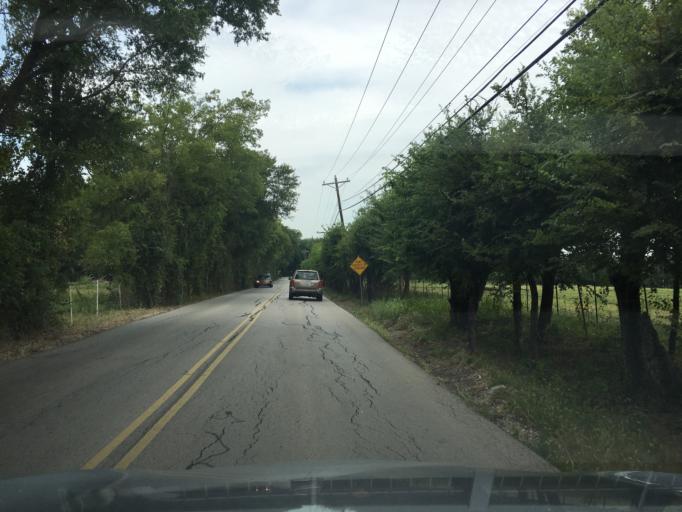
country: US
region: Texas
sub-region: Collin County
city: Saint Paul
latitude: 33.0313
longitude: -96.5782
